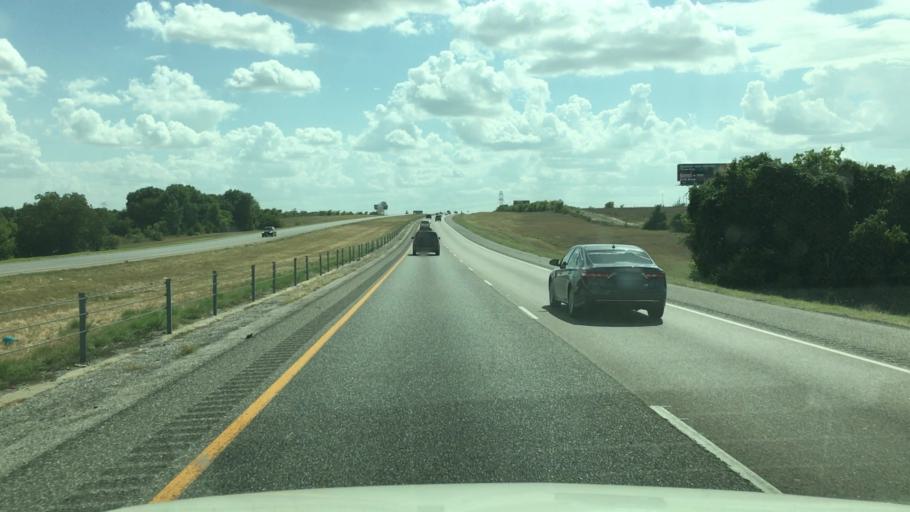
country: US
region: Texas
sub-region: Ellis County
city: Plum Grove
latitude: 32.0879
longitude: -97.0367
